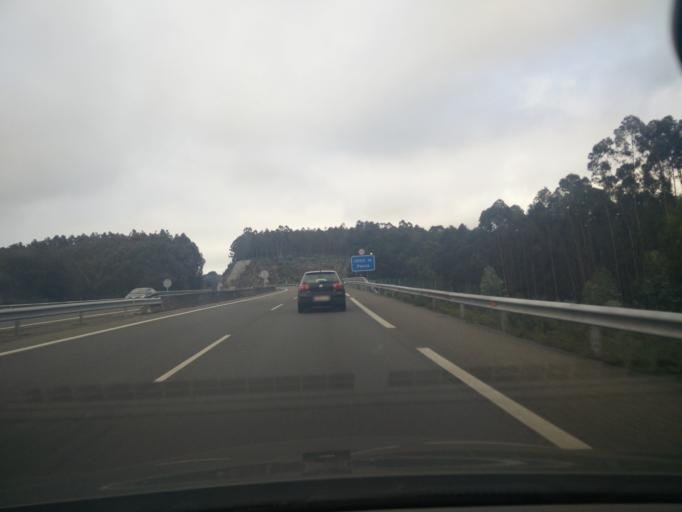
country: ES
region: Galicia
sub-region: Provincia da Coruna
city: Arteixo
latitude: 43.3200
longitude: -8.4693
